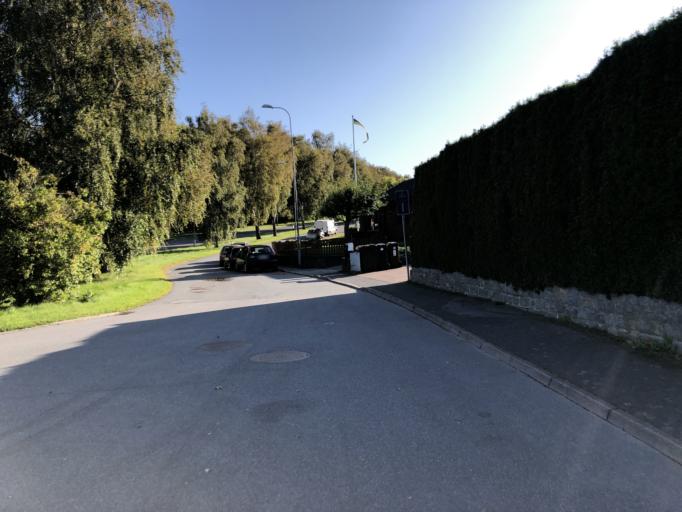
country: SE
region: Vaestra Goetaland
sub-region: Goteborg
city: Billdal
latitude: 57.6236
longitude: 11.9009
